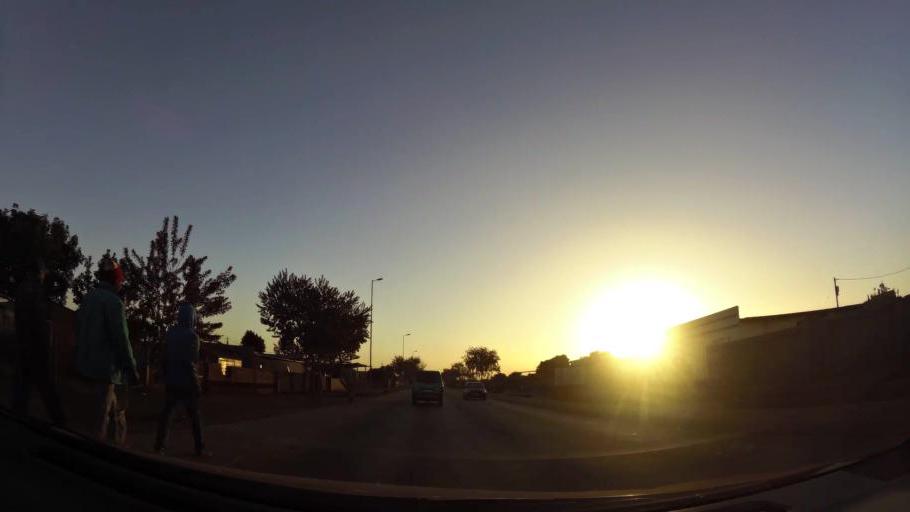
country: ZA
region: Gauteng
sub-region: City of Tshwane Metropolitan Municipality
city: Mabopane
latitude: -25.5819
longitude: 28.0818
